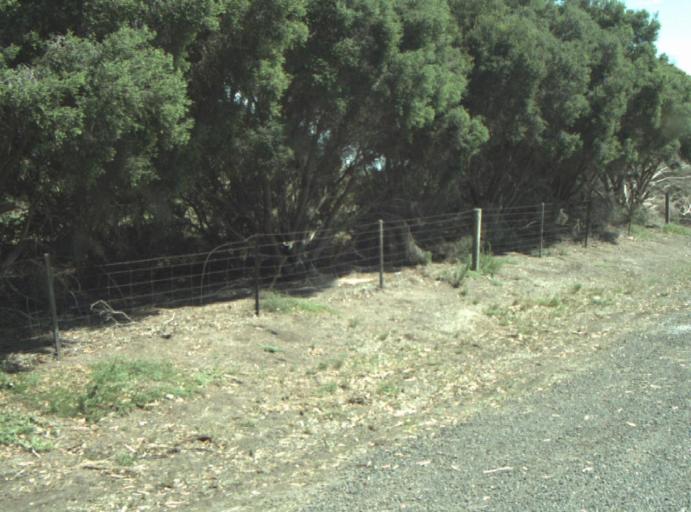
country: AU
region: Victoria
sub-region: Greater Geelong
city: Leopold
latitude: -38.1588
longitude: 144.4564
